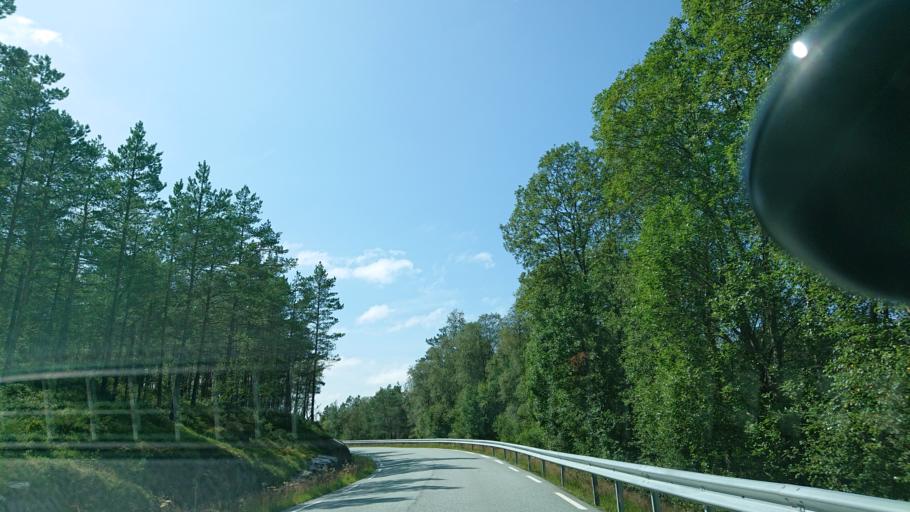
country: NO
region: Rogaland
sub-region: Hjelmeland
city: Hjelmelandsvagen
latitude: 59.2423
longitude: 6.2783
